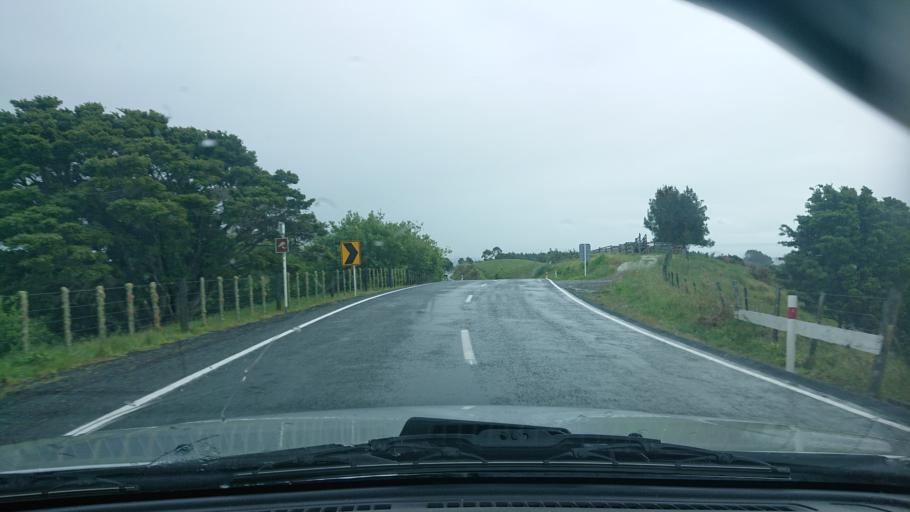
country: NZ
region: Auckland
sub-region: Auckland
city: Wellsford
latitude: -36.3536
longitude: 174.4713
